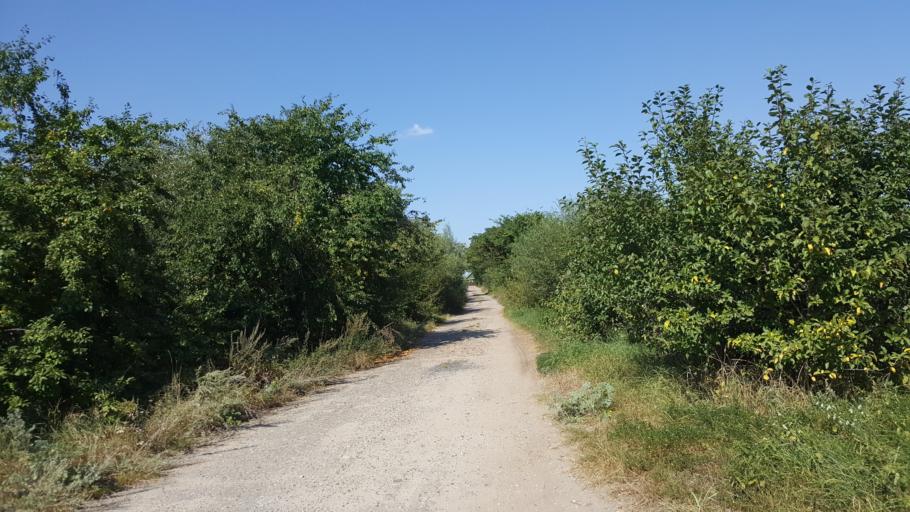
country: PL
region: Podlasie
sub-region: Powiat hajnowski
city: Czeremcha
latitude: 52.4772
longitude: 23.5442
